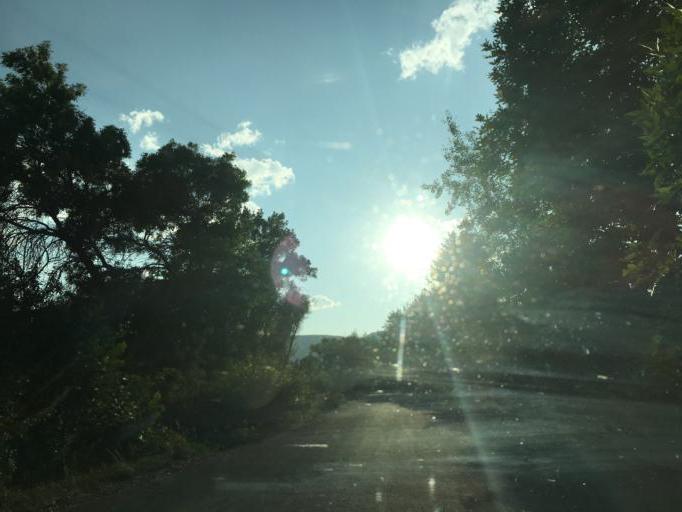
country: US
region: Colorado
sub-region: Jefferson County
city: Applewood
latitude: 39.7853
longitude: -105.1659
